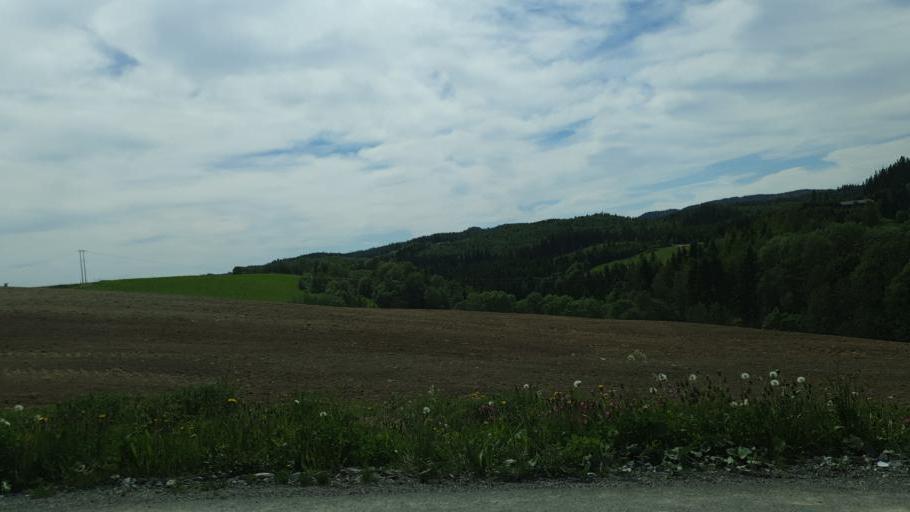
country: NO
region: Nord-Trondelag
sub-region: Leksvik
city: Leksvik
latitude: 63.6850
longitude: 10.5732
